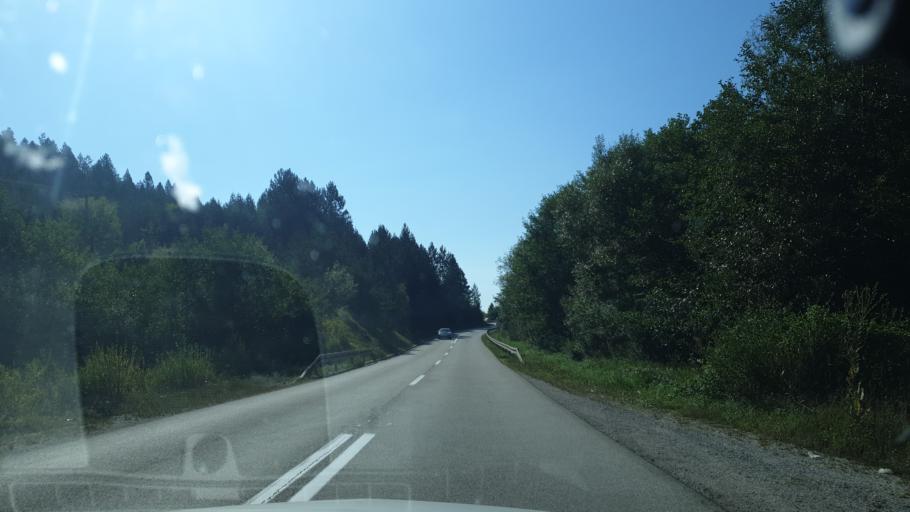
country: RS
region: Central Serbia
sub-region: Zlatiborski Okrug
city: Nova Varos
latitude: 43.5495
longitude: 19.7809
